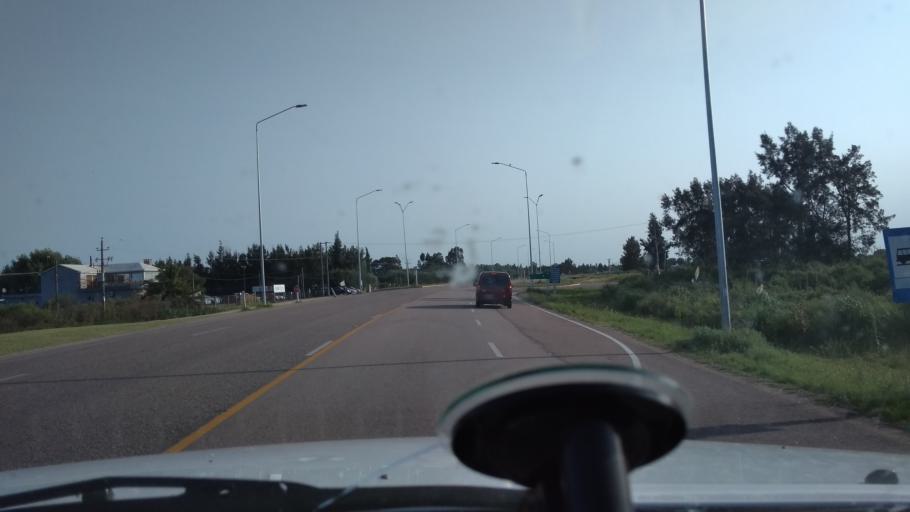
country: UY
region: Canelones
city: Sauce
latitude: -34.6479
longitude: -56.0496
